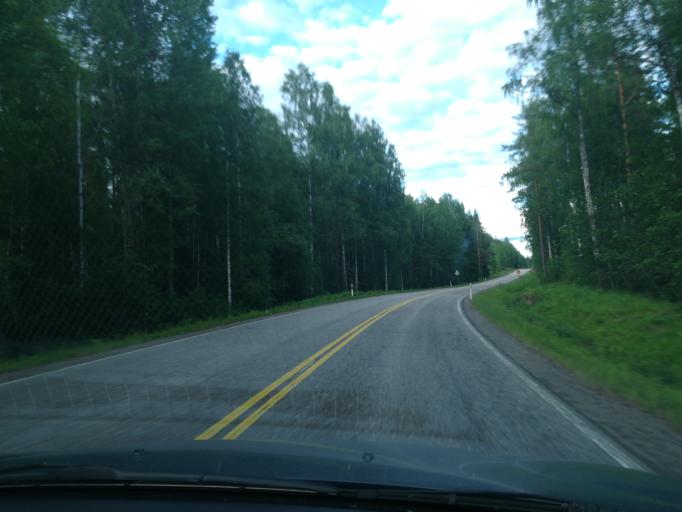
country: FI
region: Southern Savonia
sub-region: Mikkeli
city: Puumala
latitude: 61.5227
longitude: 27.9156
